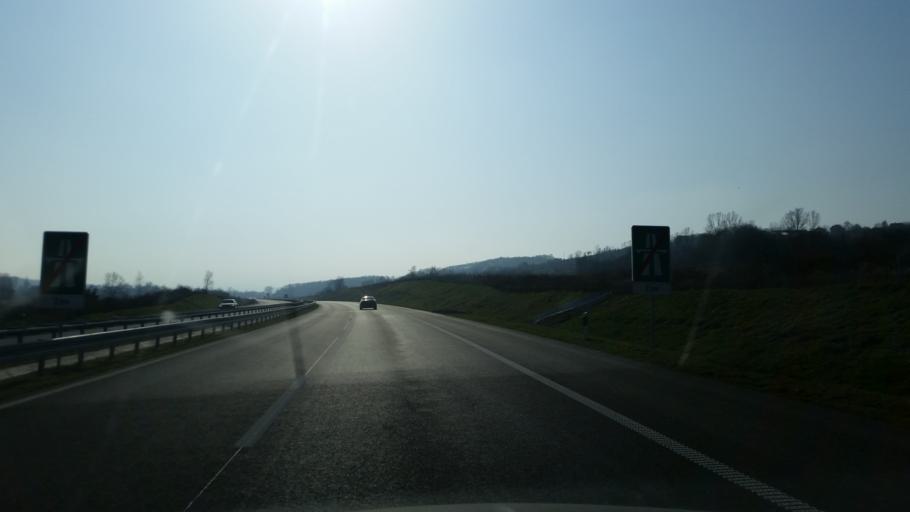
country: RS
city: Prislonica
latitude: 43.9450
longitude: 20.4000
